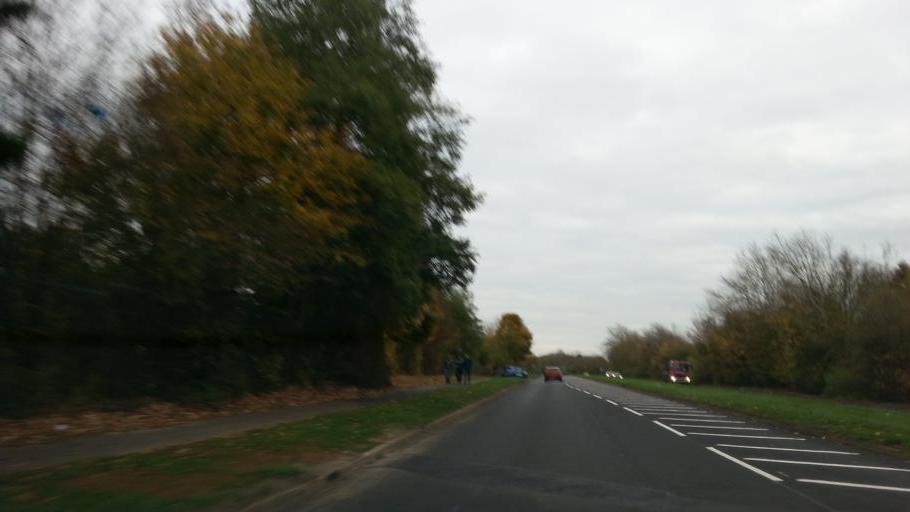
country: GB
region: England
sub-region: Northamptonshire
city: Corby
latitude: 52.4928
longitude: -0.6664
